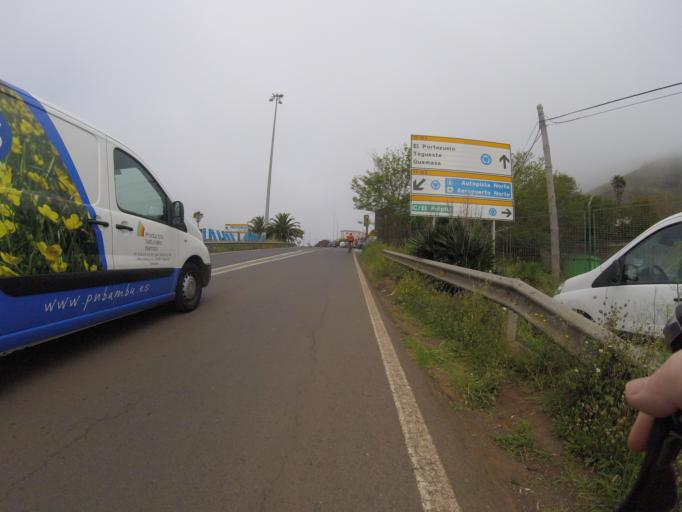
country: ES
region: Canary Islands
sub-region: Provincia de Santa Cruz de Tenerife
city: La Laguna
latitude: 28.4898
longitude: -16.3477
